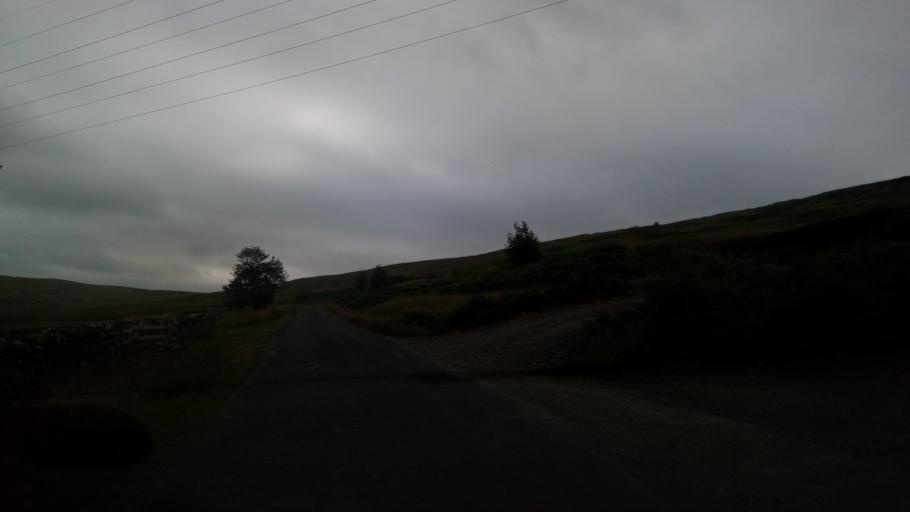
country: GB
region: Scotland
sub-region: Dumfries and Galloway
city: Langholm
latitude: 55.1572
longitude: -2.9837
